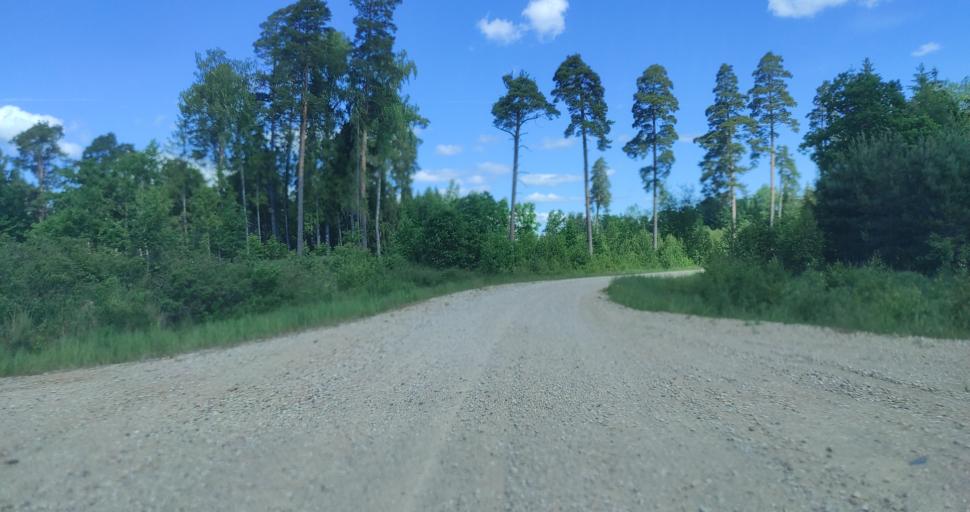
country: LV
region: Kuldigas Rajons
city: Kuldiga
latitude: 56.9442
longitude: 21.7885
